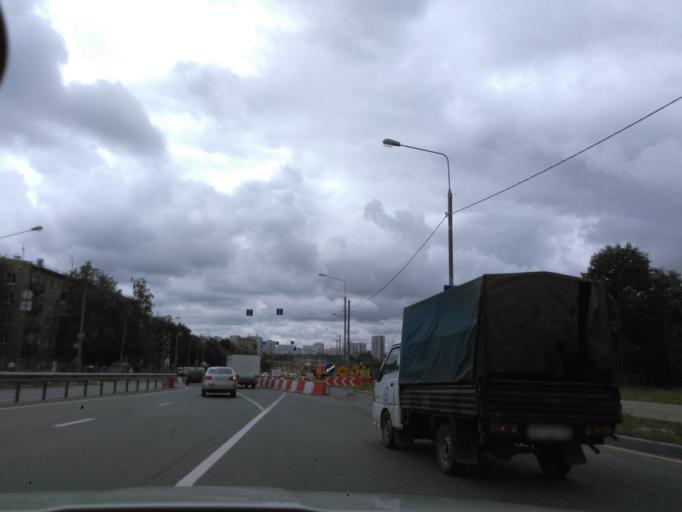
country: RU
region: Moscow
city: Davydkovo
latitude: 55.7170
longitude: 37.4518
